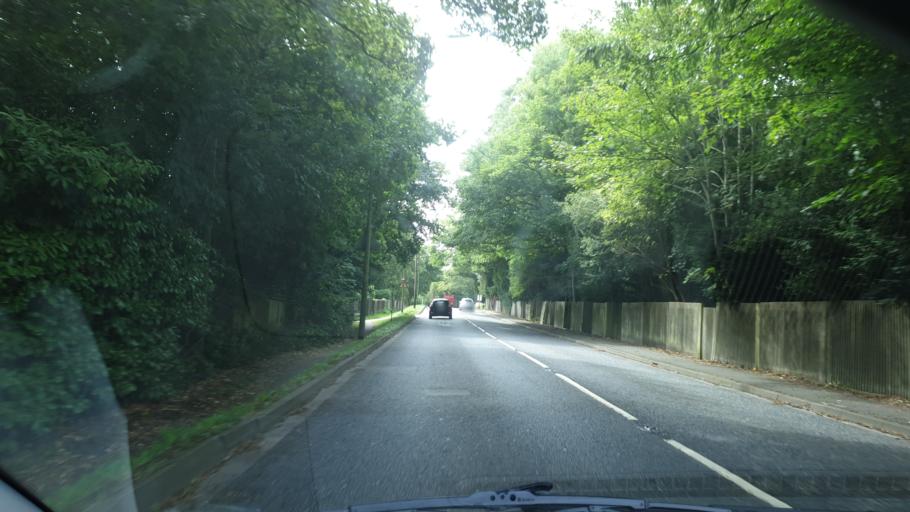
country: GB
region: England
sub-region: East Sussex
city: Forest Row
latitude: 51.0932
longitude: 0.0328
